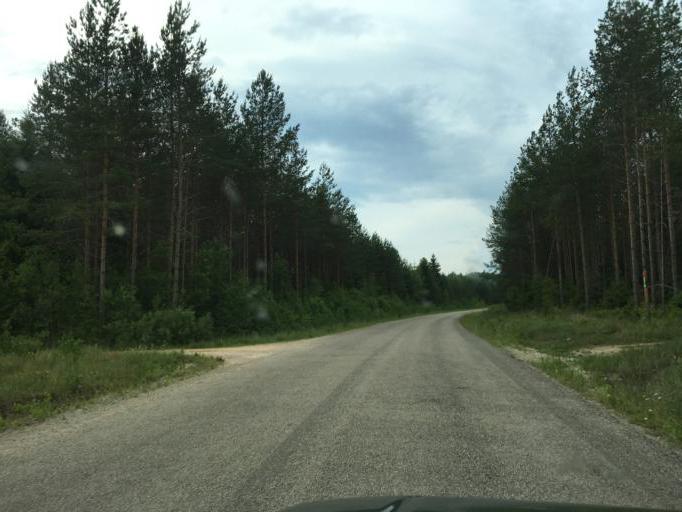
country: LV
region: Vilanu
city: Vilani
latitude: 56.7412
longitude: 27.0335
